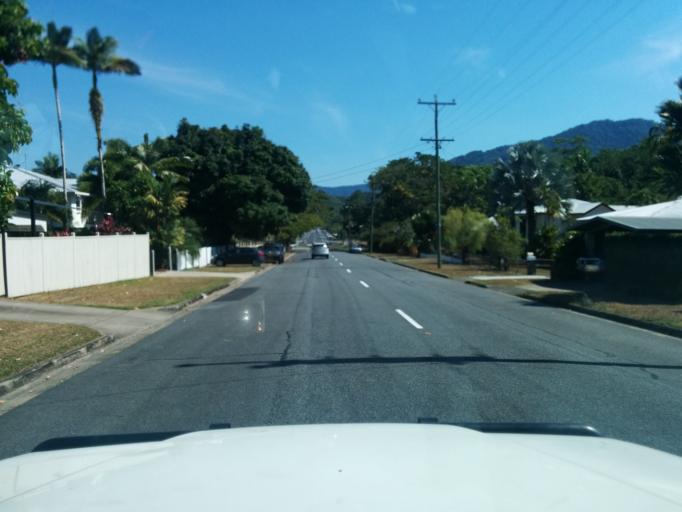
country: AU
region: Queensland
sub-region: Cairns
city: Redlynch
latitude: -16.9011
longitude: 145.7290
